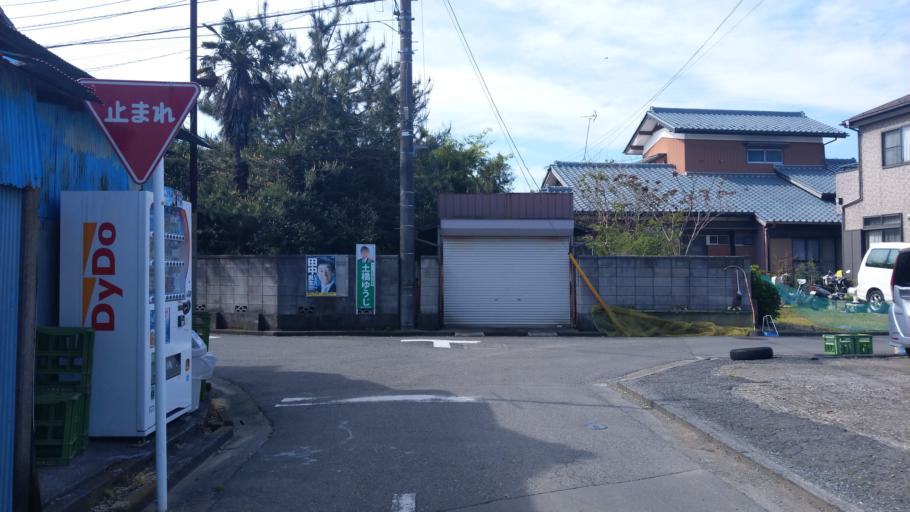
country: JP
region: Saitama
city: Yono
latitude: 35.8751
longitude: 139.5996
